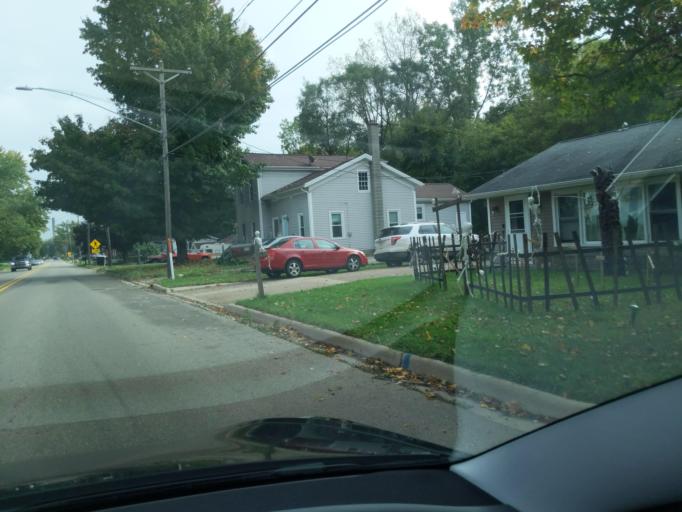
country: US
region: Michigan
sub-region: Eaton County
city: Eaton Rapids
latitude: 42.5165
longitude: -84.6631
